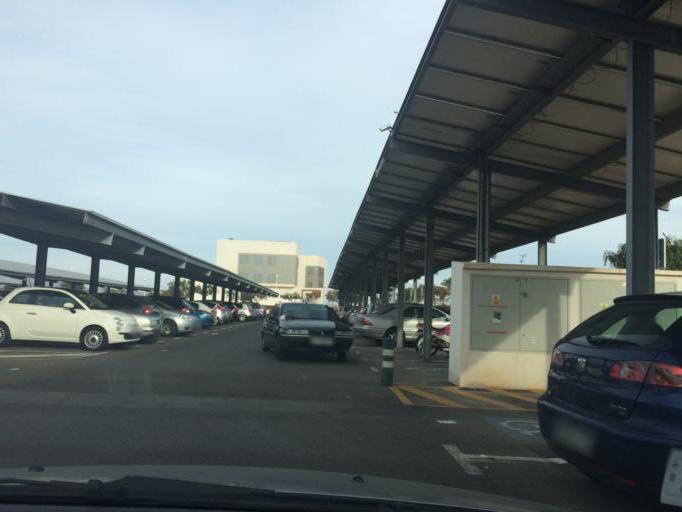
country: ES
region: Andalusia
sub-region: Provincia de Almeria
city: Almeria
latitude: 36.8315
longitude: -2.4023
